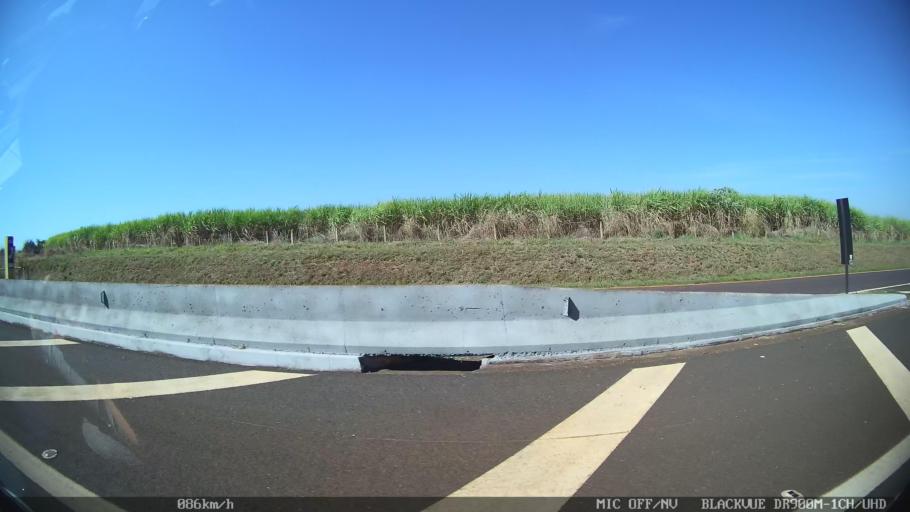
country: BR
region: Sao Paulo
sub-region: Batatais
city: Batatais
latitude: -20.8302
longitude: -47.5981
